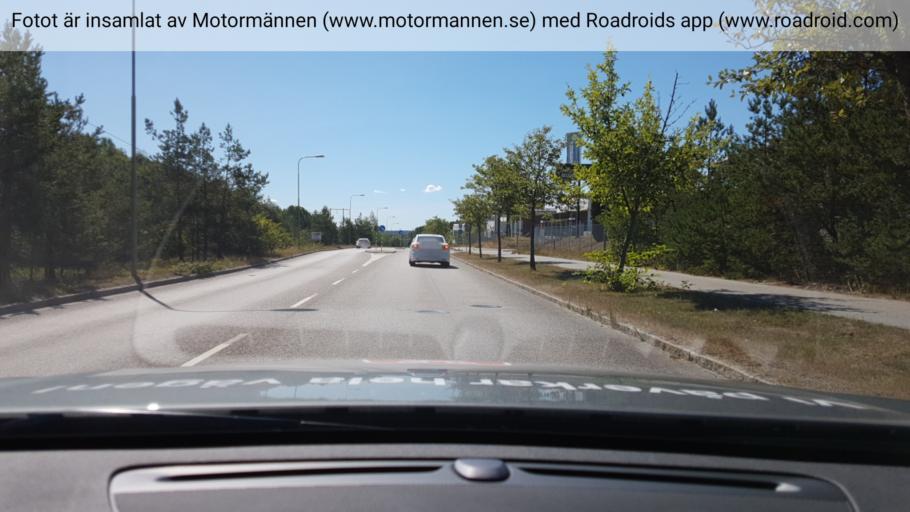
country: SE
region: Stockholm
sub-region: Nacka Kommun
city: Alta
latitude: 59.2405
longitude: 18.1952
